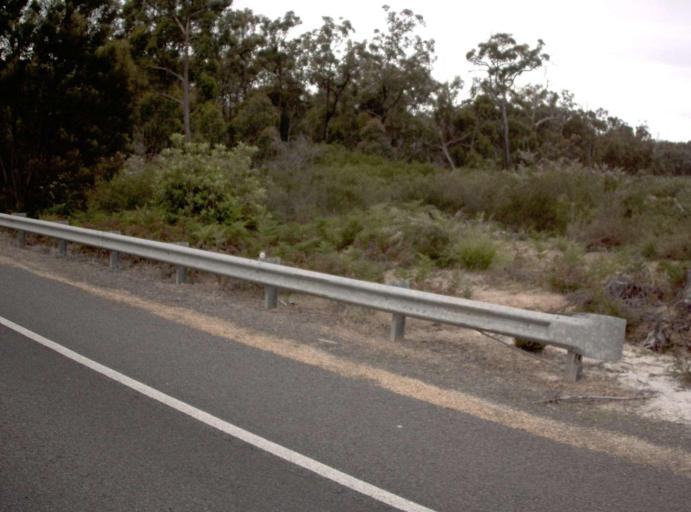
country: AU
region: Victoria
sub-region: Wellington
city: Sale
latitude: -38.3332
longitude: 147.0166
